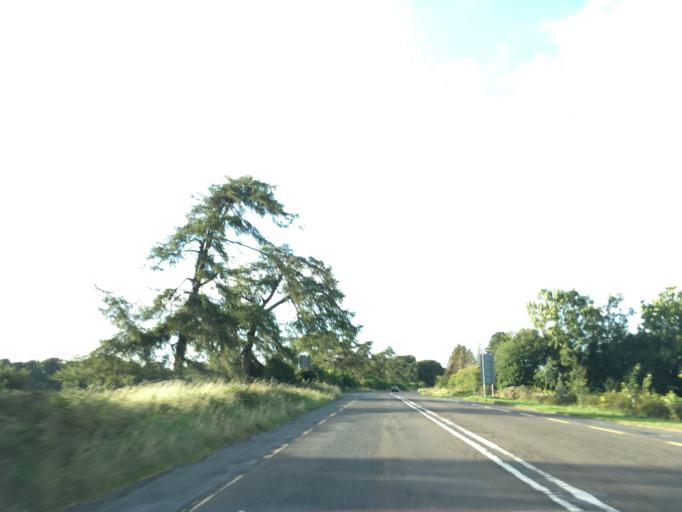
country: IE
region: Munster
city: Cashel
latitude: 52.4783
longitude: -7.8921
